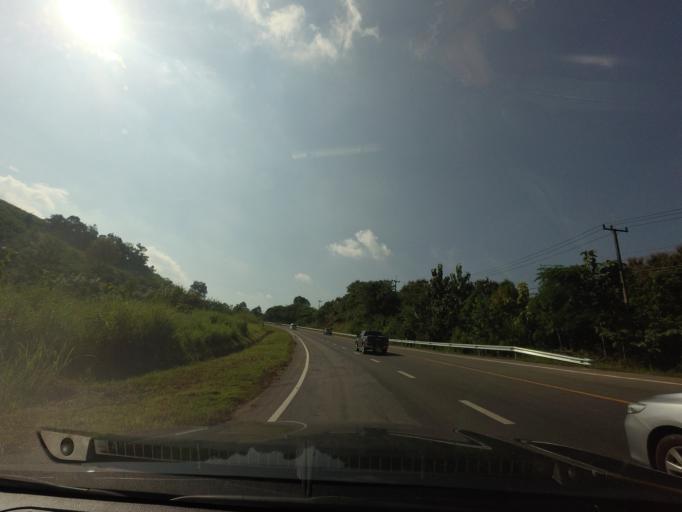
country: TH
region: Nan
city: Santi Suk
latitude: 18.9274
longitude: 100.8996
